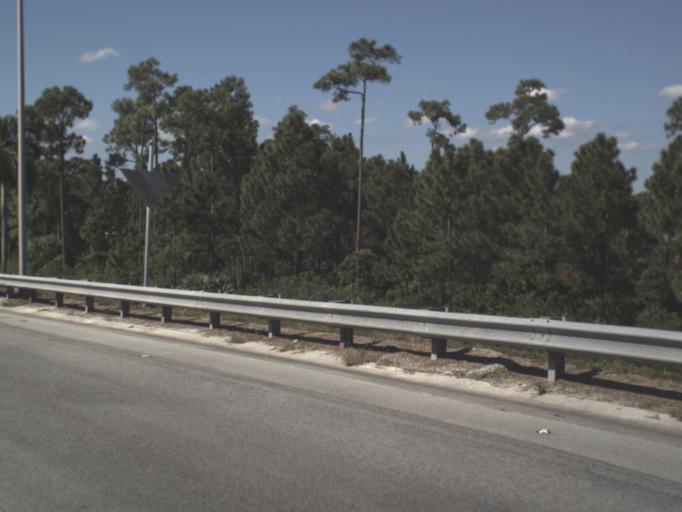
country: US
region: Florida
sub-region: Miami-Dade County
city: Leisure City
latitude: 25.4766
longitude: -80.4416
